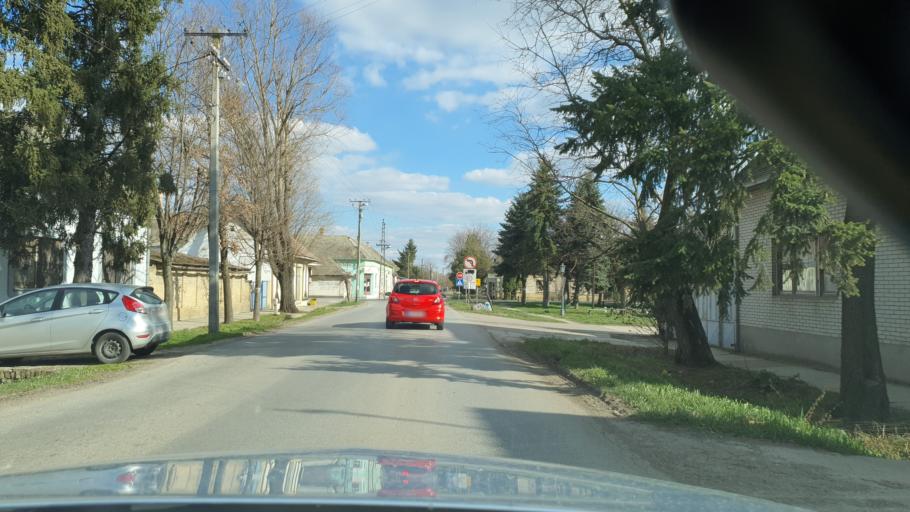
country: RS
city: Zmajevo
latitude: 45.4561
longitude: 19.6862
